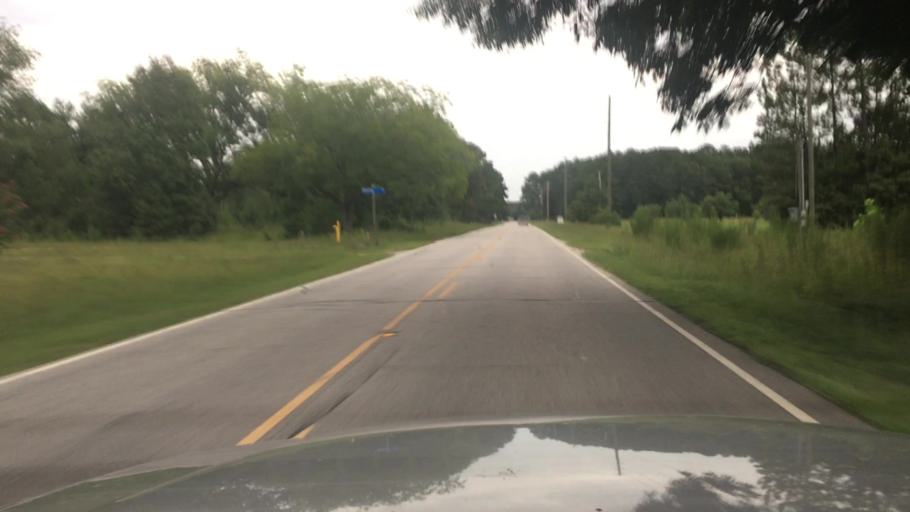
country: US
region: North Carolina
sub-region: Hoke County
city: Rockfish
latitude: 34.9818
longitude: -79.0430
